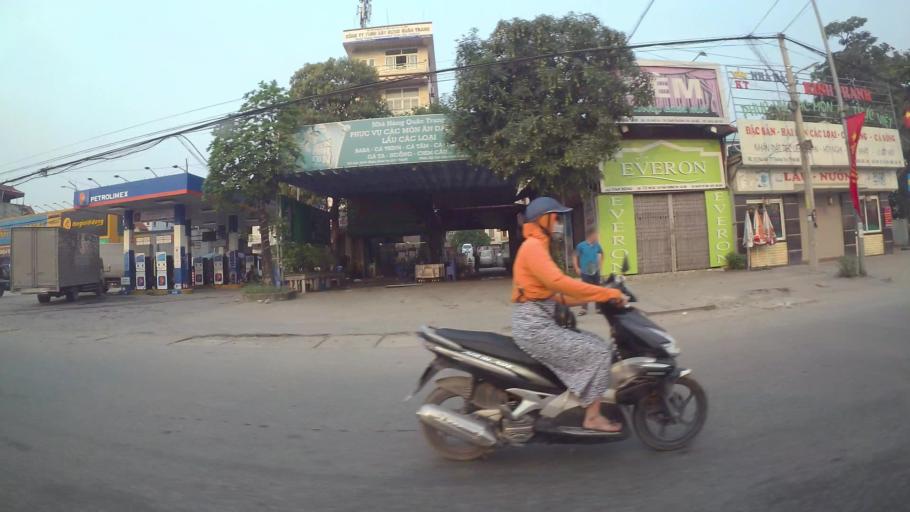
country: VN
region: Ha Noi
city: Thuong Tin
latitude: 20.8736
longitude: 105.8634
